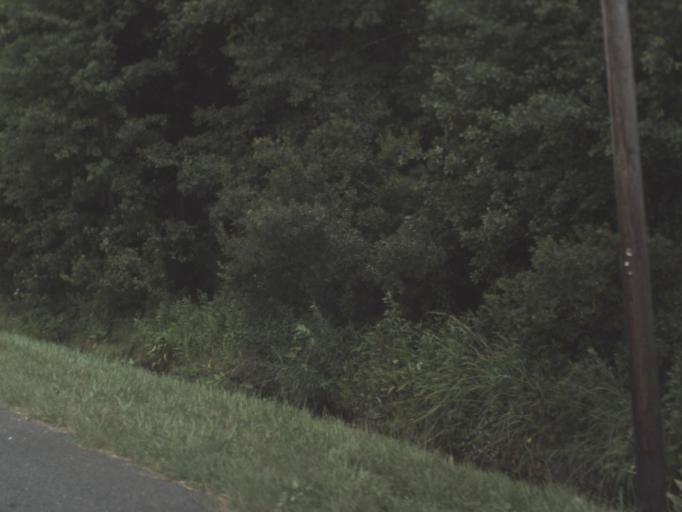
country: US
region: Florida
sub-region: Union County
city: Lake Butler
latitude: 29.9413
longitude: -82.4243
